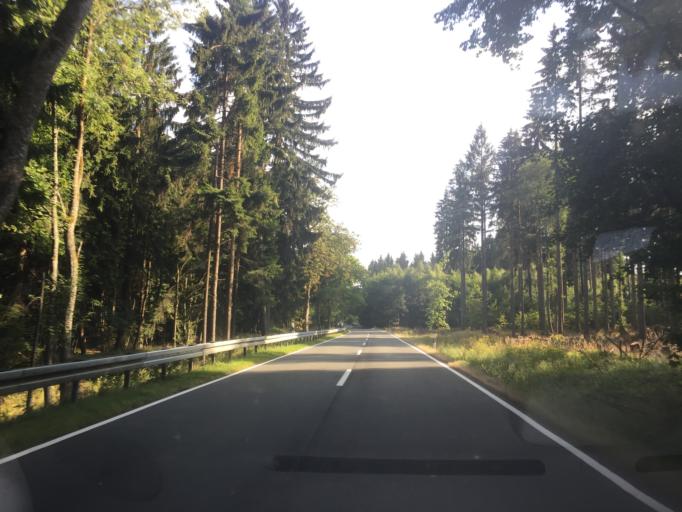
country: DE
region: Saxony-Anhalt
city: Darlingerode
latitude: 51.7757
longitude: 10.7305
